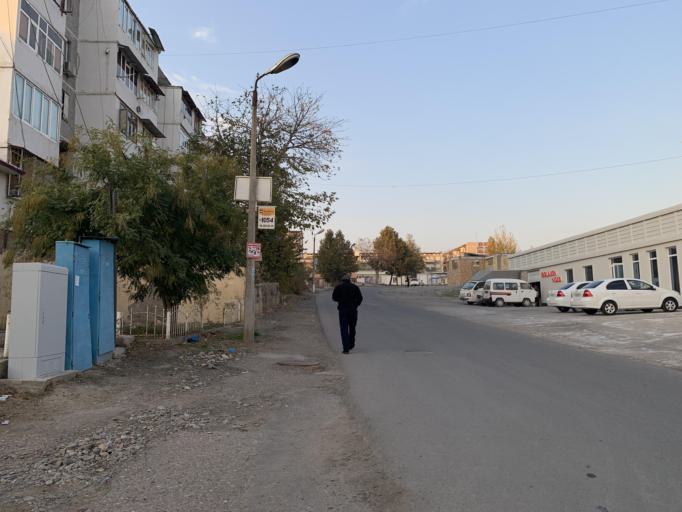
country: UZ
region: Namangan
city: Namangan Shahri
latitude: 41.0038
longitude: 71.5989
